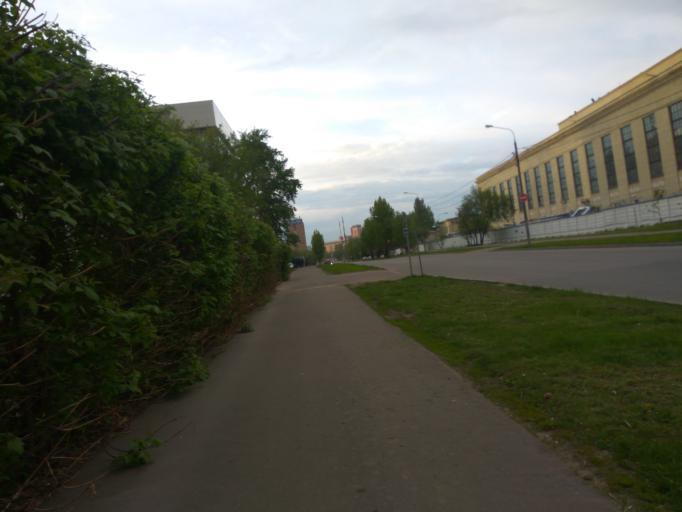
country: RU
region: Moscow
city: Sokol
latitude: 55.7824
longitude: 37.5007
